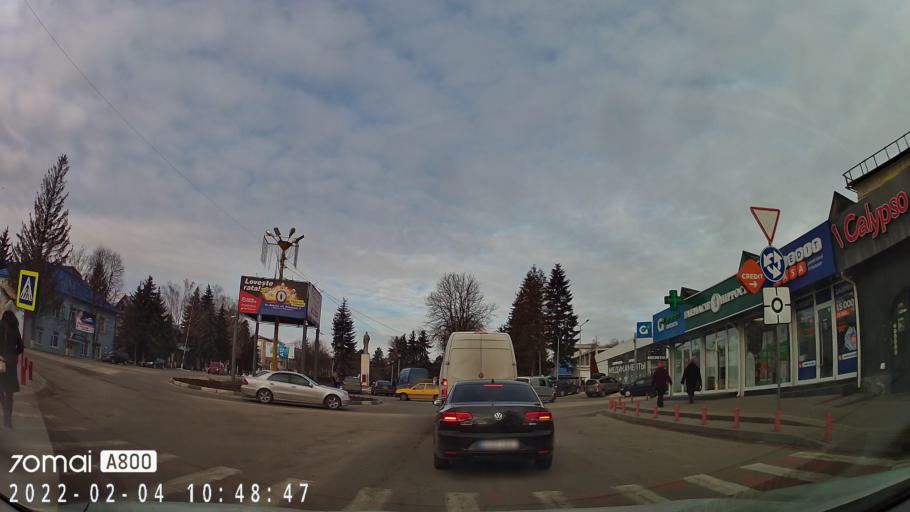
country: MD
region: Briceni
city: Briceni
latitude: 48.3591
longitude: 27.0896
